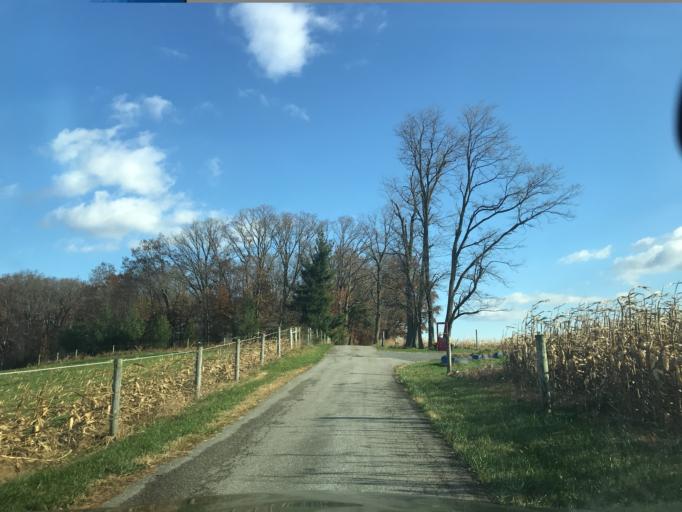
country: US
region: Maryland
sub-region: Carroll County
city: Taneytown
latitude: 39.6296
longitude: -77.0950
